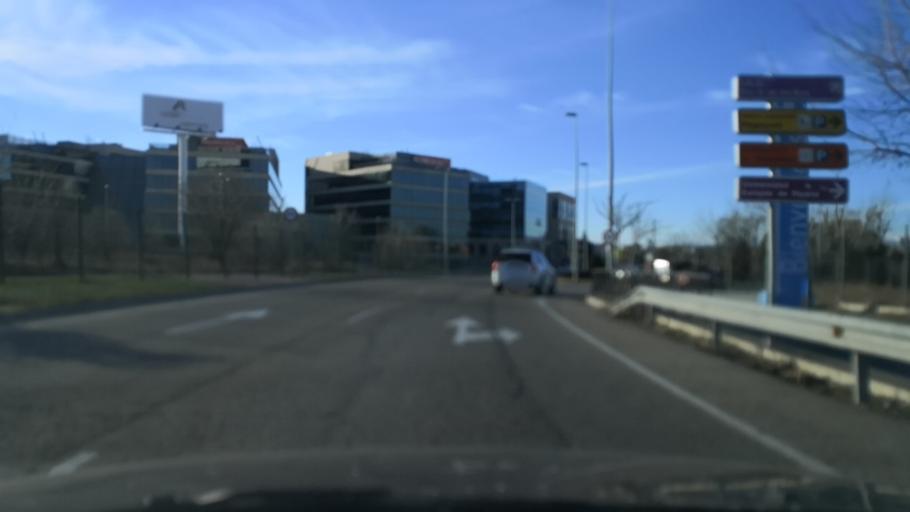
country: ES
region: Madrid
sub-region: Provincia de Madrid
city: San Sebastian de los Reyes
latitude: 40.5337
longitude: -3.6188
